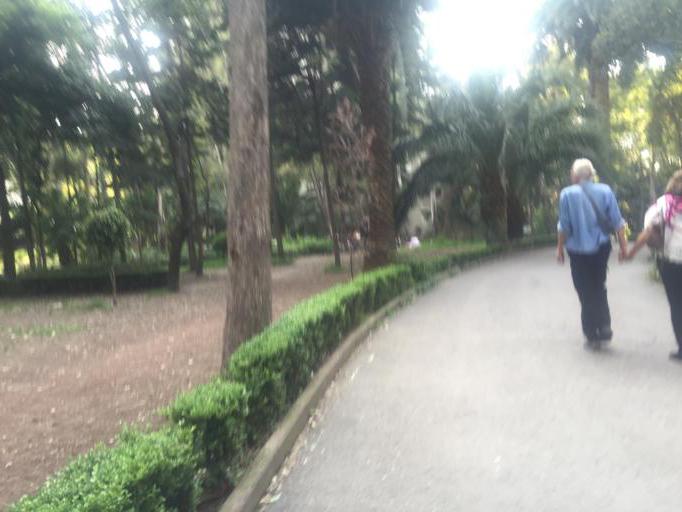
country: MX
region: Mexico City
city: Colonia del Valle
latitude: 19.3774
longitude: -99.1791
